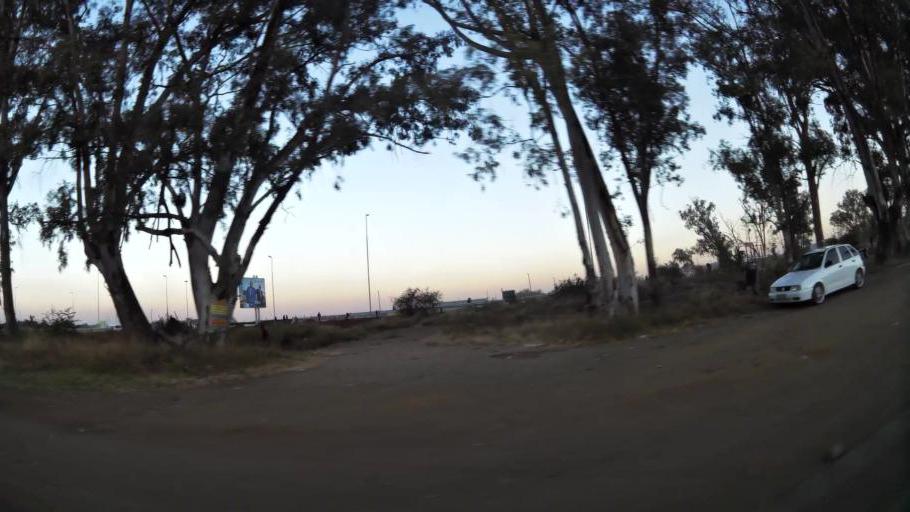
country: ZA
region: North-West
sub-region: Bojanala Platinum District Municipality
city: Rustenburg
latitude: -25.6610
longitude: 27.2342
